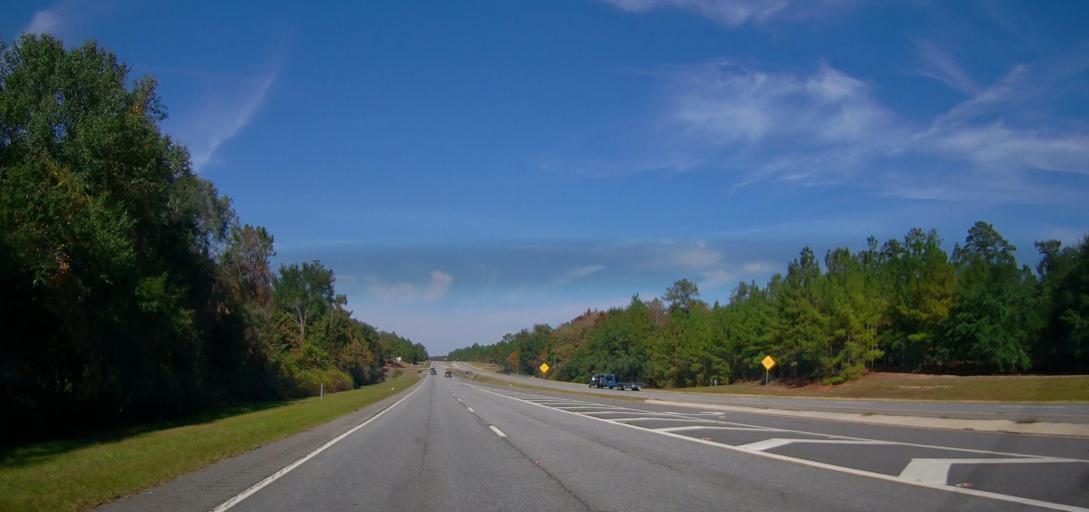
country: US
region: Georgia
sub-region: Lee County
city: Leesburg
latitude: 31.7161
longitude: -83.9889
